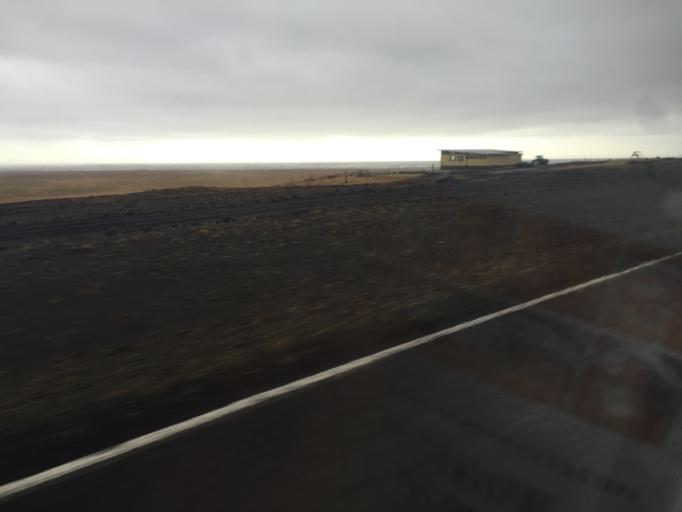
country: IS
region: East
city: Hoefn
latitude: 63.8788
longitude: -16.6634
